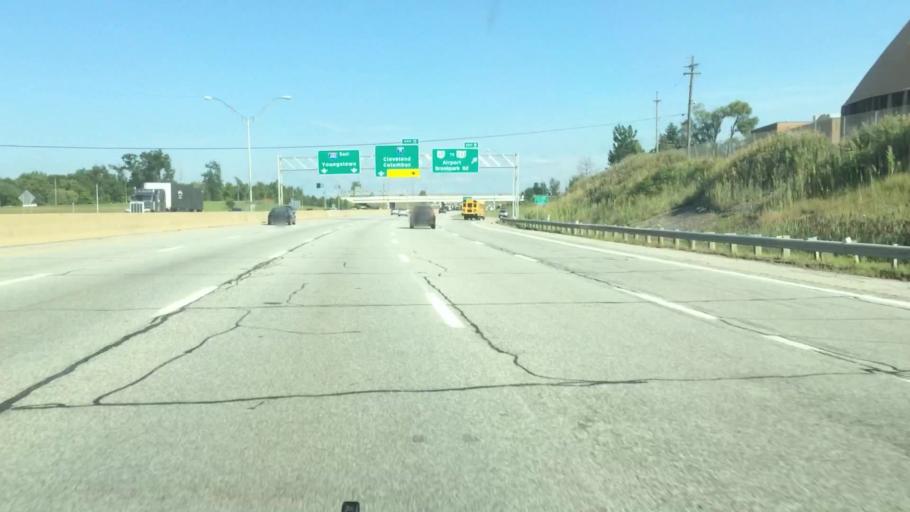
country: US
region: Ohio
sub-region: Cuyahoga County
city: Fairview Park
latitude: 41.4234
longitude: -81.8482
